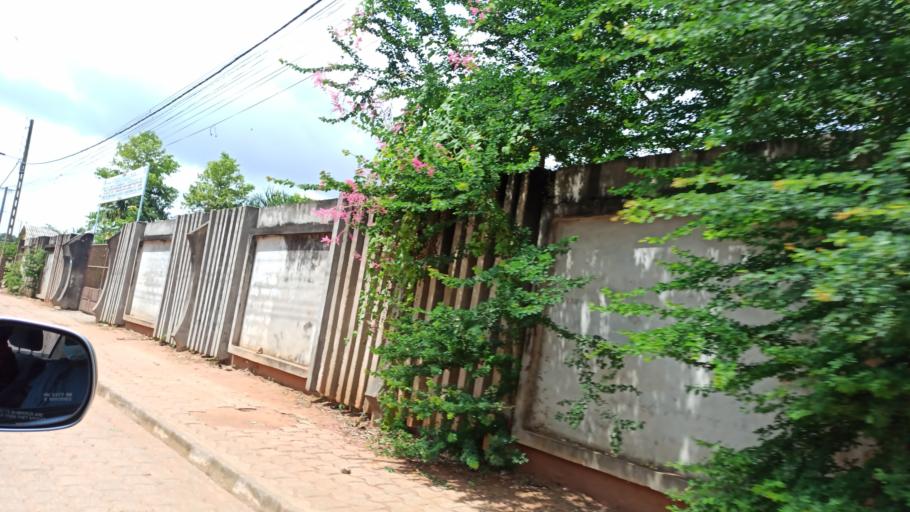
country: BJ
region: Queme
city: Porto-Novo
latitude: 6.4751
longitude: 2.6164
